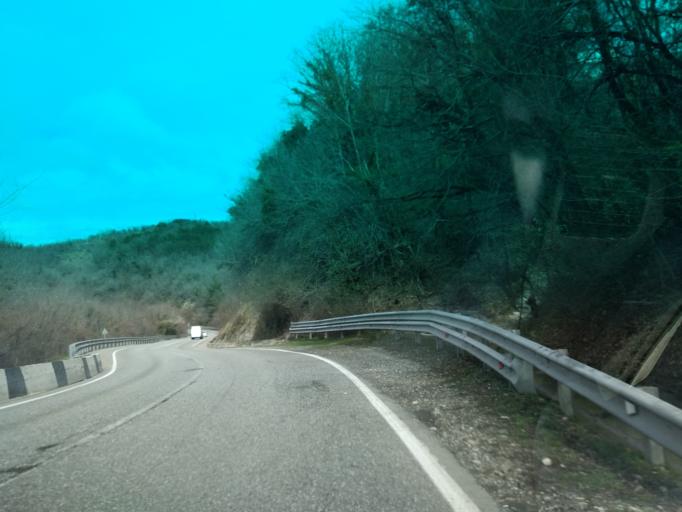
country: RU
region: Krasnodarskiy
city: Shepsi
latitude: 44.0461
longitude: 39.1336
